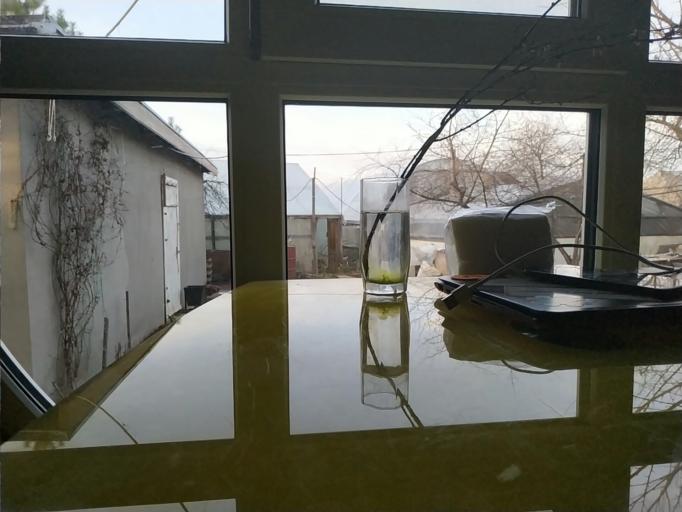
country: RU
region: Republic of Karelia
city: Suoyarvi
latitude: 62.3203
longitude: 32.0632
